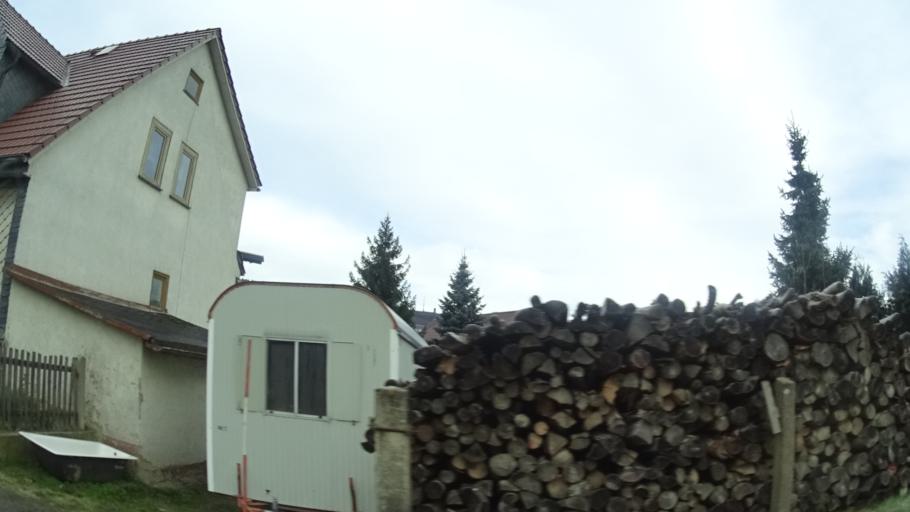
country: DE
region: Thuringia
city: Brotterode
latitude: 50.8236
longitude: 10.4499
